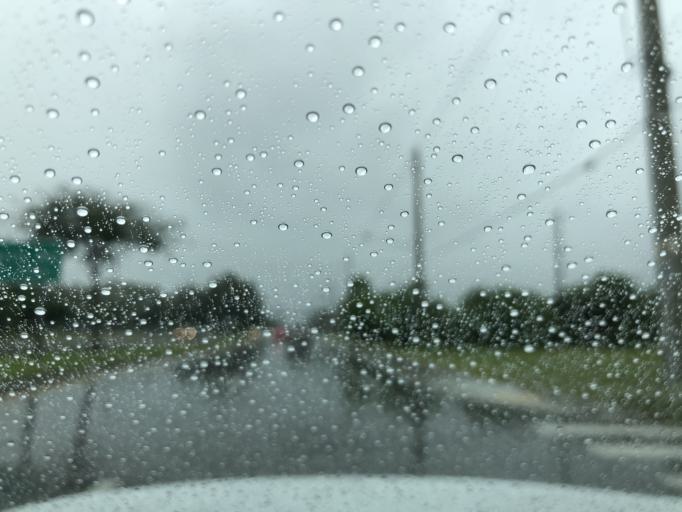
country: US
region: Florida
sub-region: Palm Beach County
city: Royal Palm Estates
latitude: 26.6795
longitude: -80.1202
